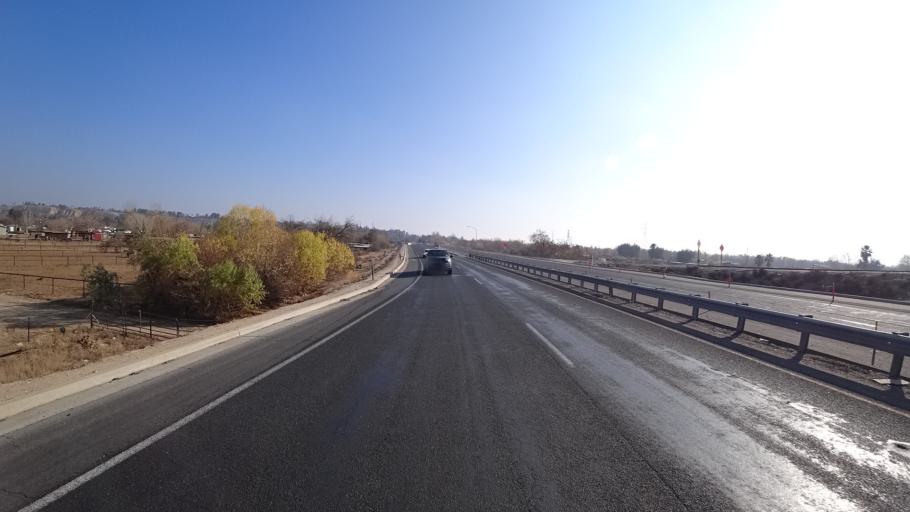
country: US
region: California
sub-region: Kern County
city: Oildale
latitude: 35.4102
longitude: -119.0121
